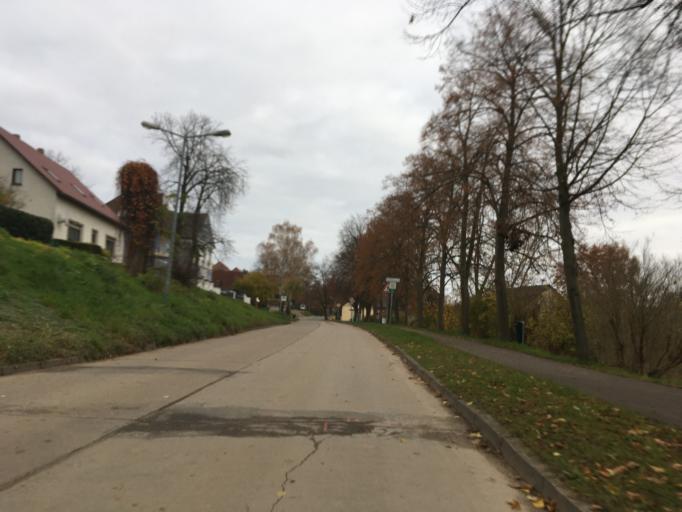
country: DE
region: Brandenburg
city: Frankfurt (Oder)
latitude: 52.3133
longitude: 14.5393
